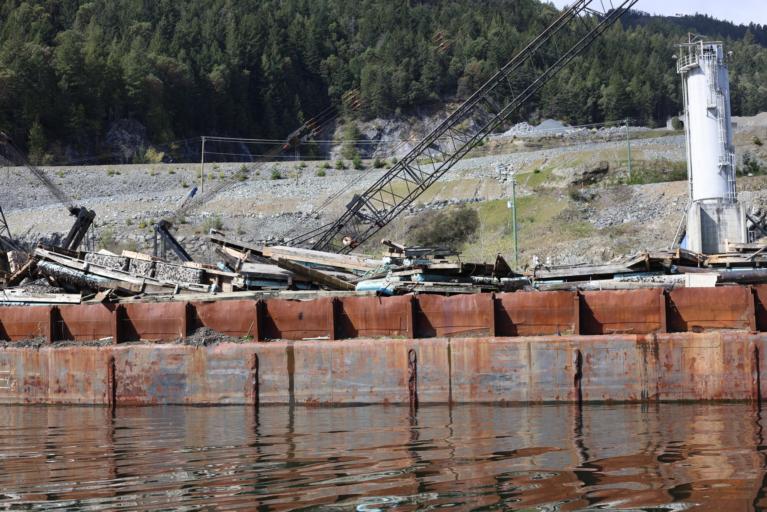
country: CA
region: British Columbia
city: North Saanich
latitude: 48.5860
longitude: -123.5202
